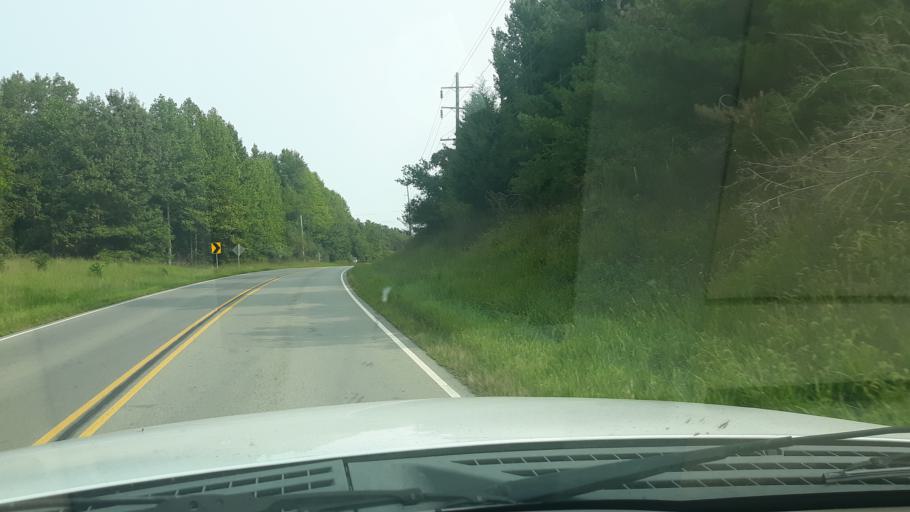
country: US
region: Illinois
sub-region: White County
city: Norris City
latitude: 37.9240
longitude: -88.3502
